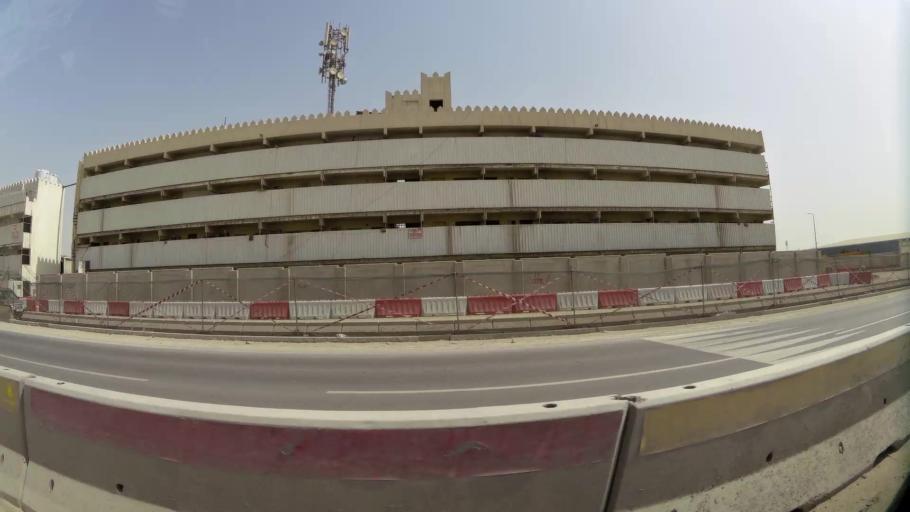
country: QA
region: Baladiyat ar Rayyan
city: Ar Rayyan
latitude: 25.1867
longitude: 51.4225
